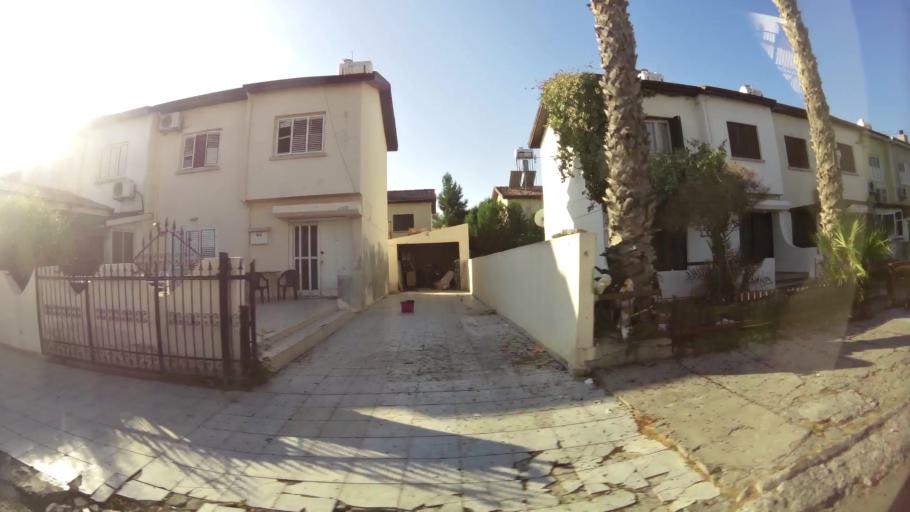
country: CY
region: Lefkosia
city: Nicosia
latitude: 35.2064
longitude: 33.3497
